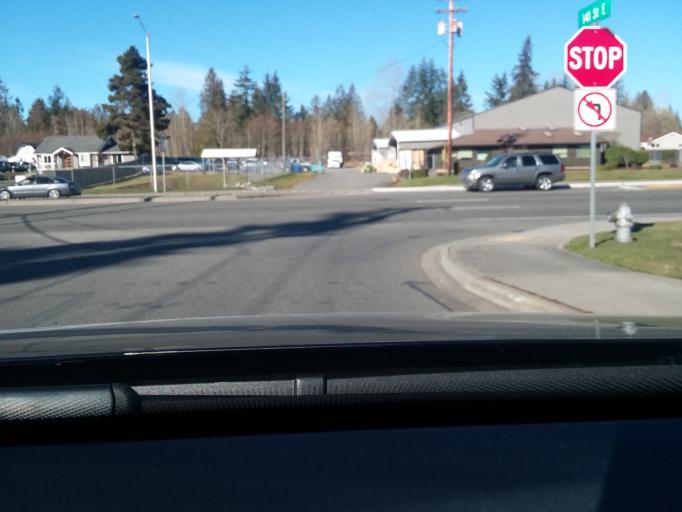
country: US
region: Washington
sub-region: Pierce County
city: Frederickson
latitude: 47.1282
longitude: -122.3571
